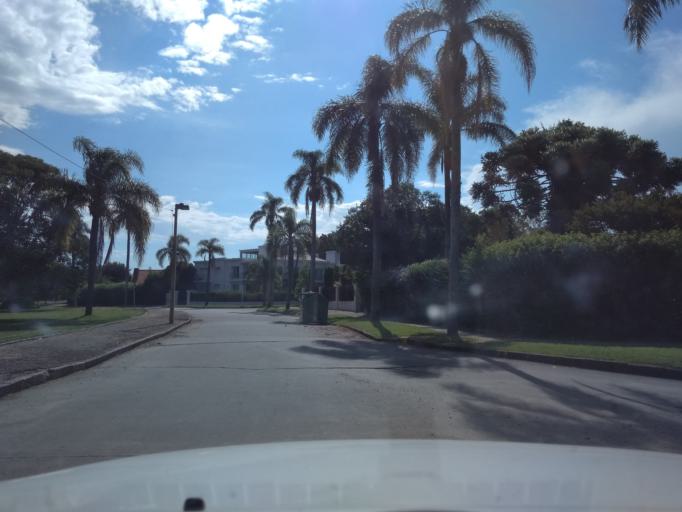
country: UY
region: Canelones
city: Paso de Carrasco
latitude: -34.8902
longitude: -56.0659
